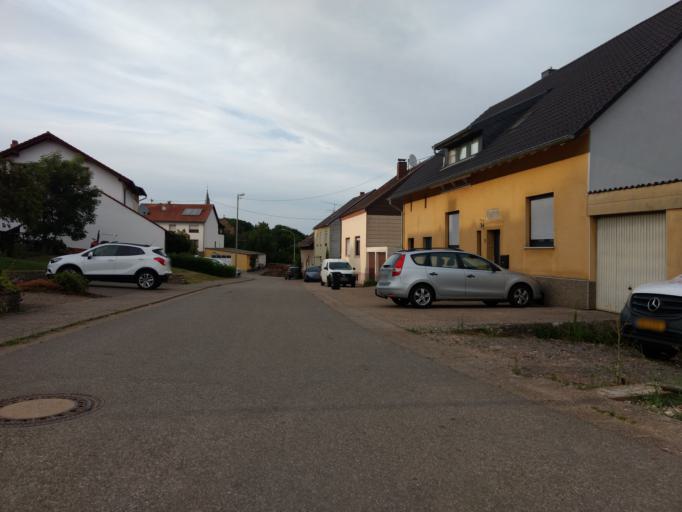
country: FR
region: Lorraine
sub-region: Departement de la Moselle
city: Bouzonville
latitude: 49.3213
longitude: 6.6007
